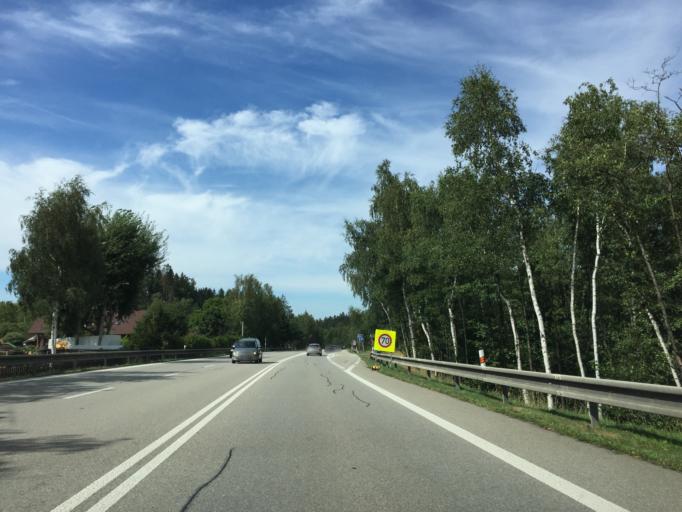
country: CZ
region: Central Bohemia
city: Votice
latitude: 49.6164
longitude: 14.6592
